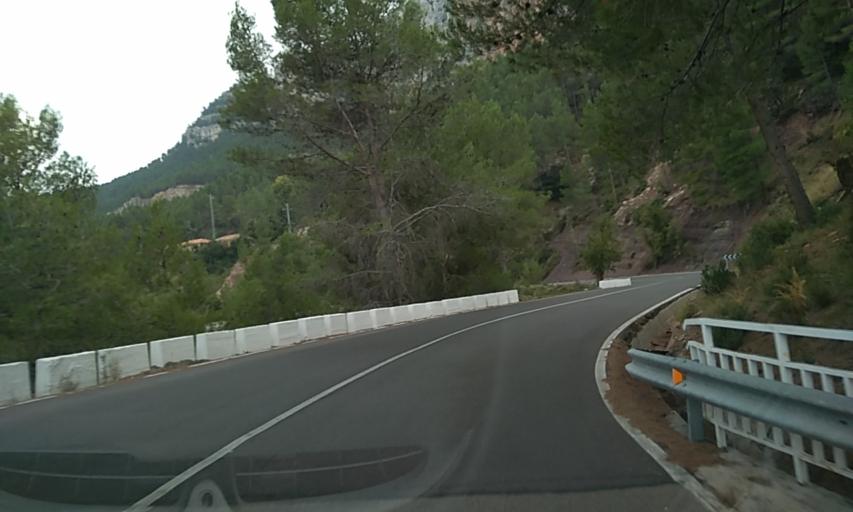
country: ES
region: Valencia
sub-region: Provincia de Castello
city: Puebla de Arenoso
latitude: 40.0860
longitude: -0.5551
